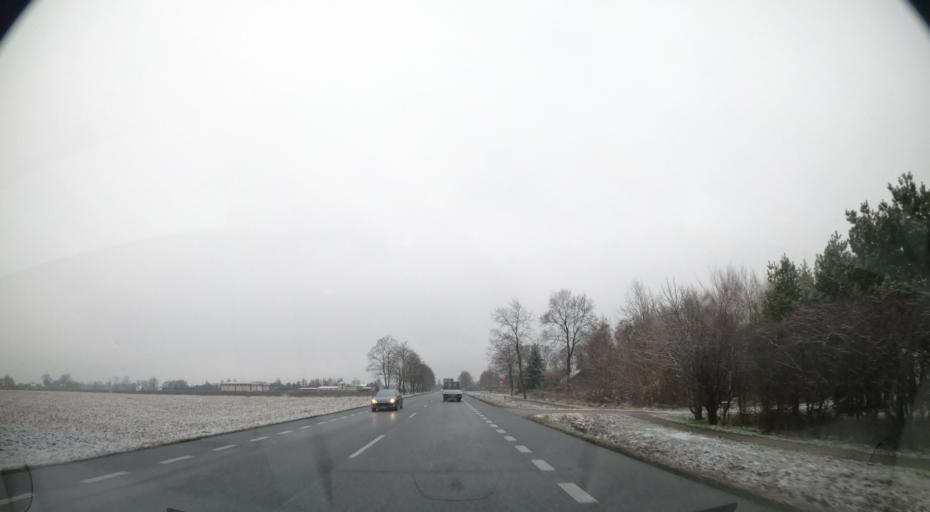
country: PL
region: Masovian Voivodeship
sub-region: Powiat sochaczewski
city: Paprotnia
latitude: 52.2100
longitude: 20.4512
